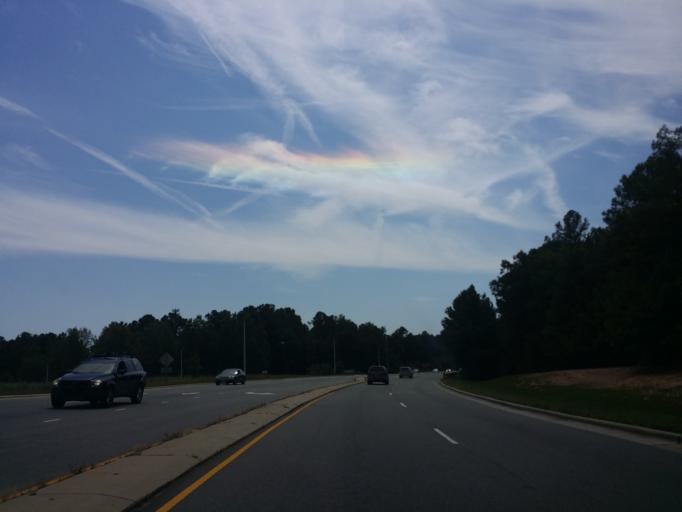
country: US
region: North Carolina
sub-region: Wake County
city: Morrisville
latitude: 35.8542
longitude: -78.7965
